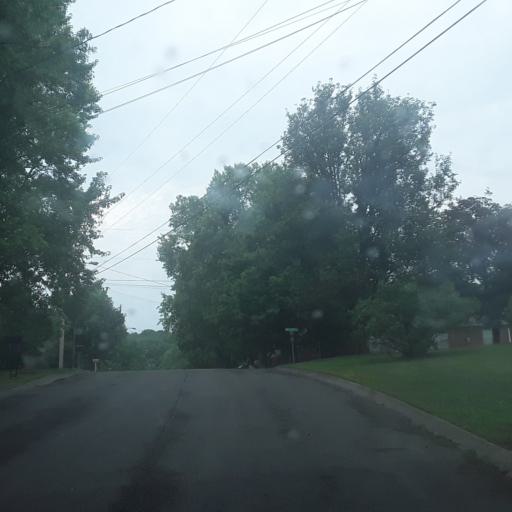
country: US
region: Tennessee
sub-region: Williamson County
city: Brentwood
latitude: 36.0573
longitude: -86.7302
